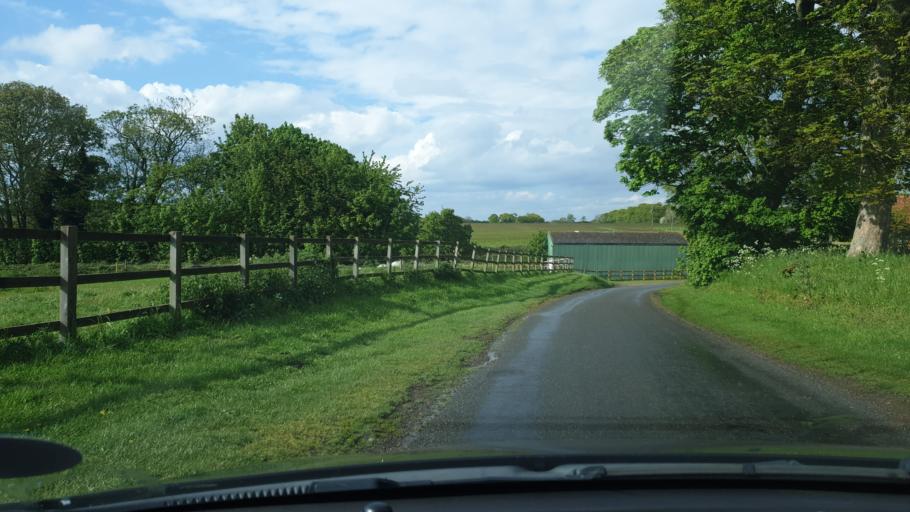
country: GB
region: England
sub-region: Essex
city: Saint Osyth
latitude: 51.8211
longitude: 1.0756
